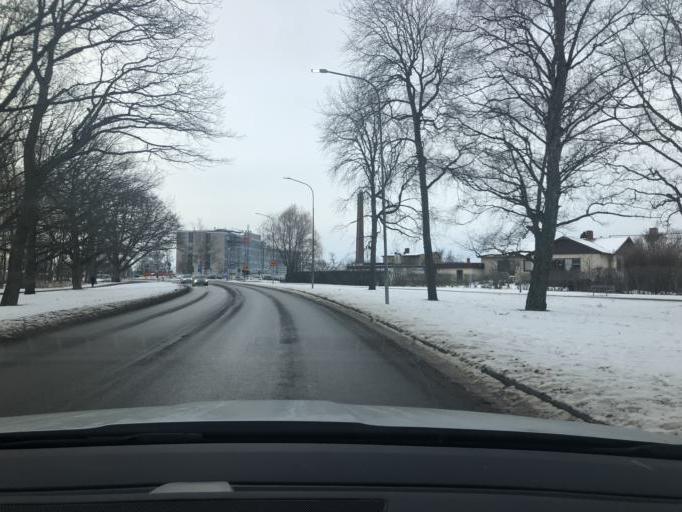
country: SE
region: OEstergoetland
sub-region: Motala Kommun
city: Motala
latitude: 58.5473
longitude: 15.0295
